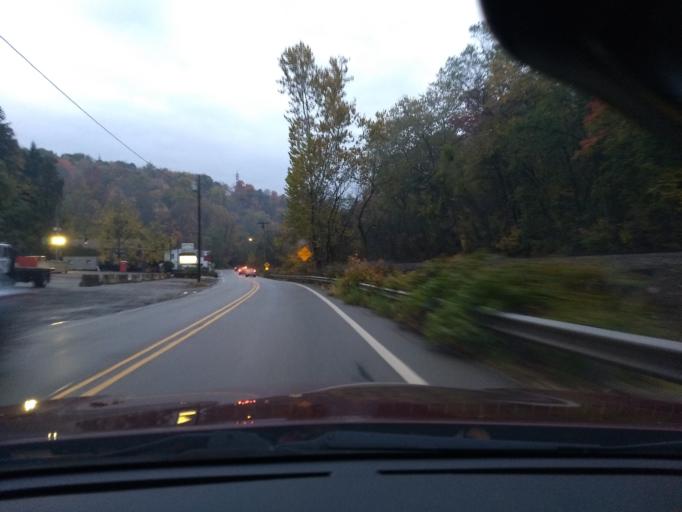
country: US
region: Pennsylvania
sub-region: Allegheny County
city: Brentwood
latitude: 40.3642
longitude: -79.9495
